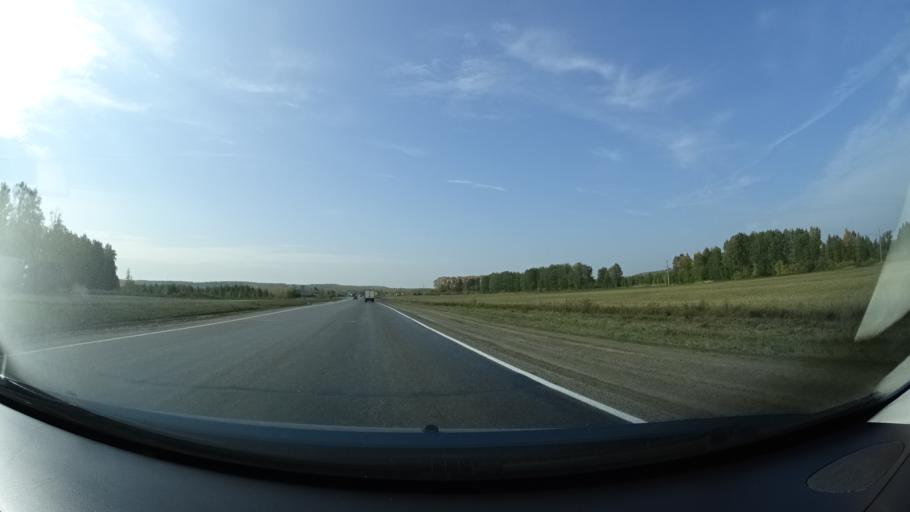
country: RU
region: Bashkortostan
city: Kandry
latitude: 54.6083
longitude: 54.3092
